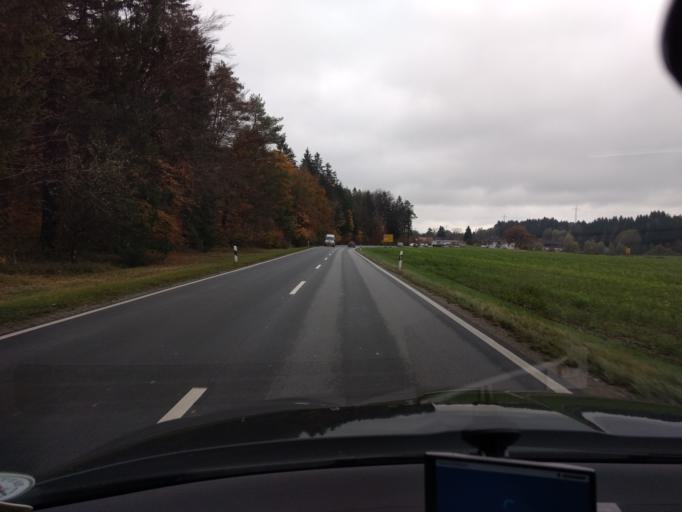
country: DE
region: Bavaria
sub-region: Upper Bavaria
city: Geretsried
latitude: 47.8654
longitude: 11.4688
